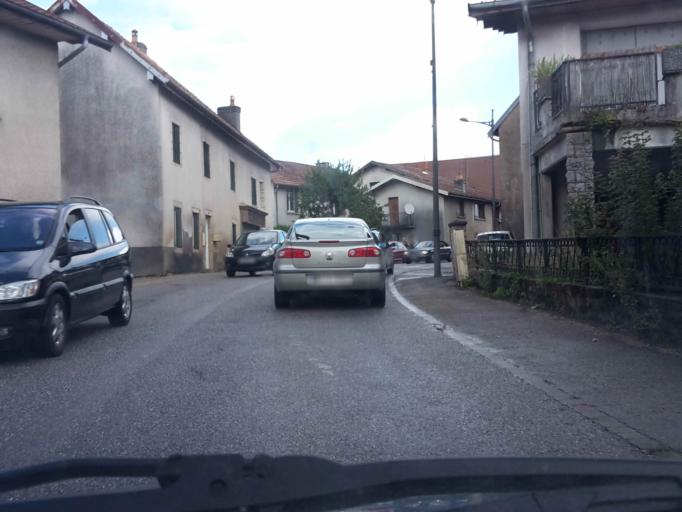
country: FR
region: Franche-Comte
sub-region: Departement du Doubs
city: Nancray
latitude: 47.2452
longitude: 6.1835
